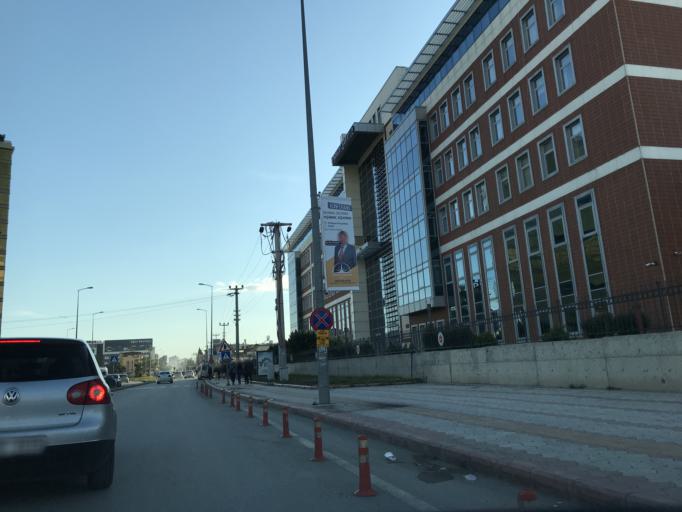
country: TR
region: Hatay
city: Iskenderun
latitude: 36.5745
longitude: 36.1599
